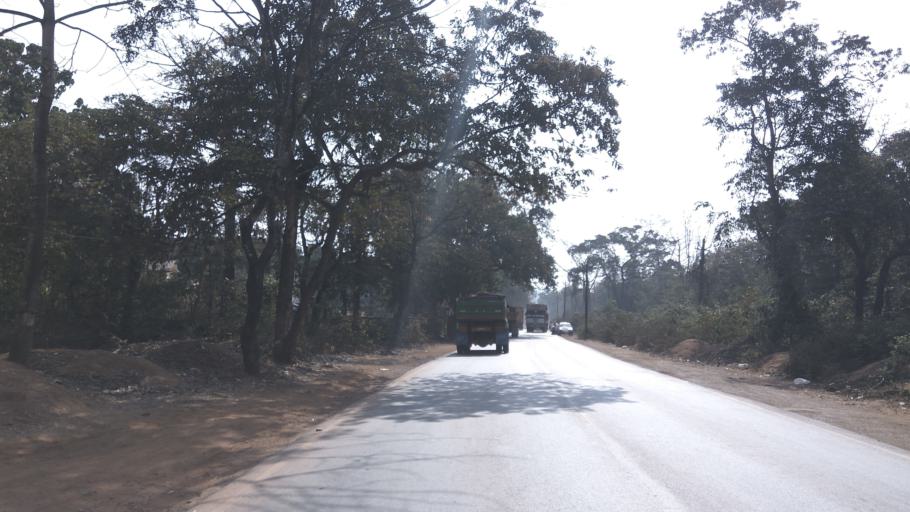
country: IN
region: Goa
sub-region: North Goa
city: Palle
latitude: 15.3951
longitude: 74.1169
